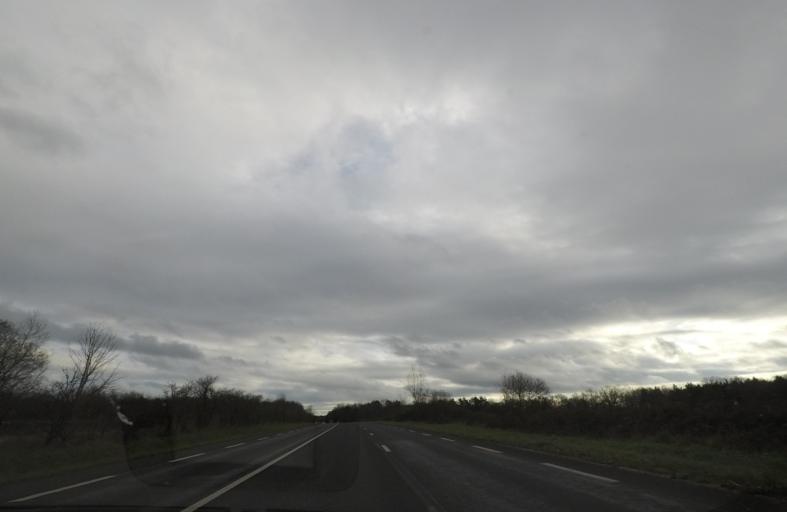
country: FR
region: Centre
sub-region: Departement du Loir-et-Cher
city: Mur-de-Sologne
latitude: 47.3979
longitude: 1.6394
